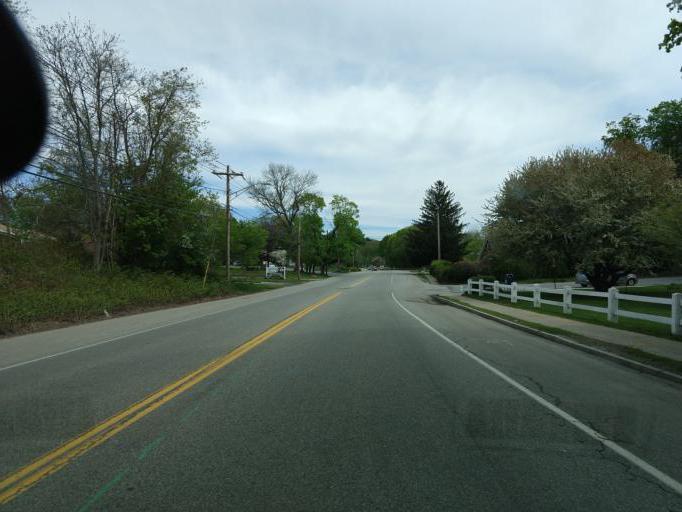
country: US
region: Massachusetts
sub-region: Essex County
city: Haverhill
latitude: 42.7879
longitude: -71.0709
